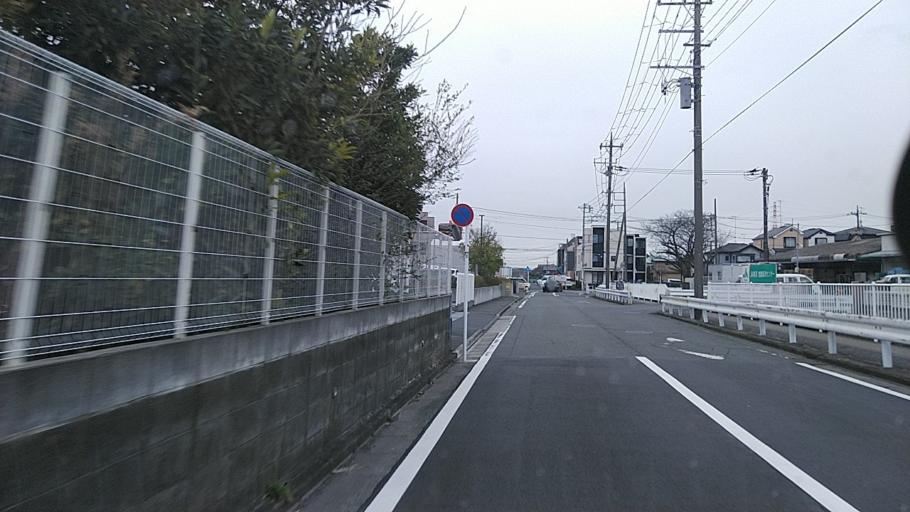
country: JP
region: Kanagawa
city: Fujisawa
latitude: 35.4110
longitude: 139.5026
